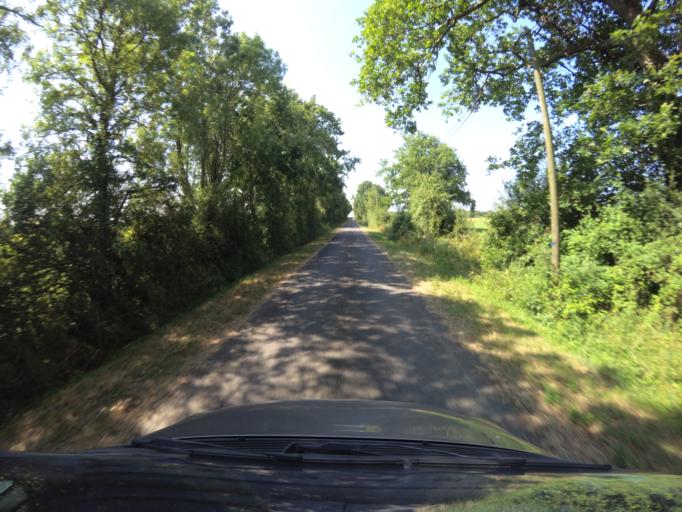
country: FR
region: Pays de la Loire
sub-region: Departement de la Loire-Atlantique
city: Vieillevigne
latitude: 46.9799
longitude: -1.4570
